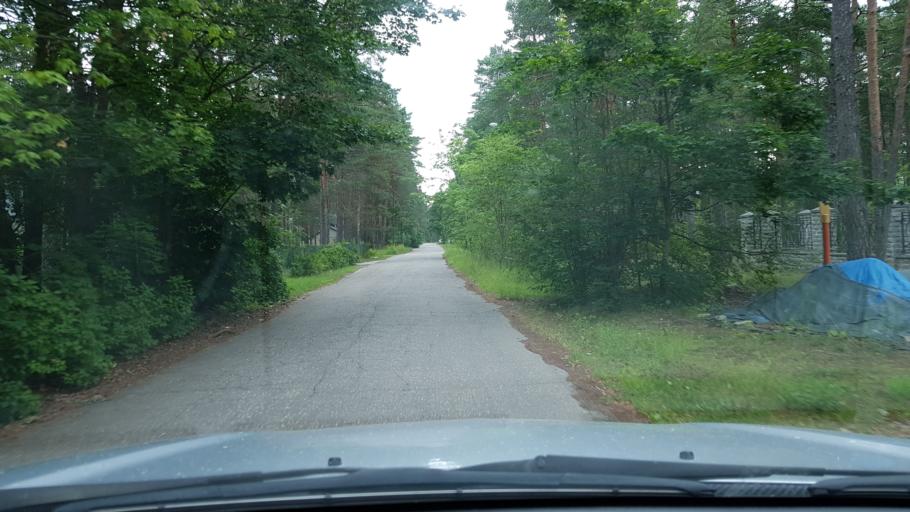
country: EE
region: Ida-Virumaa
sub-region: Narva-Joesuu linn
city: Narva-Joesuu
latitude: 59.4528
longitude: 28.0587
